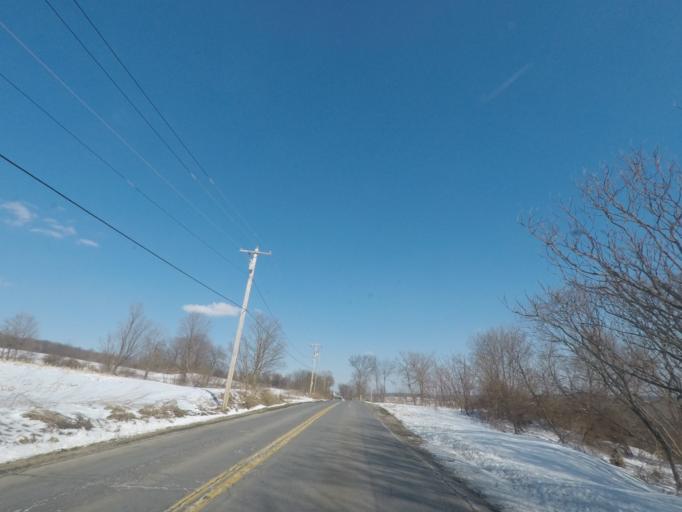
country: US
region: New York
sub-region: Saratoga County
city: Stillwater
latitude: 42.9135
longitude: -73.5579
